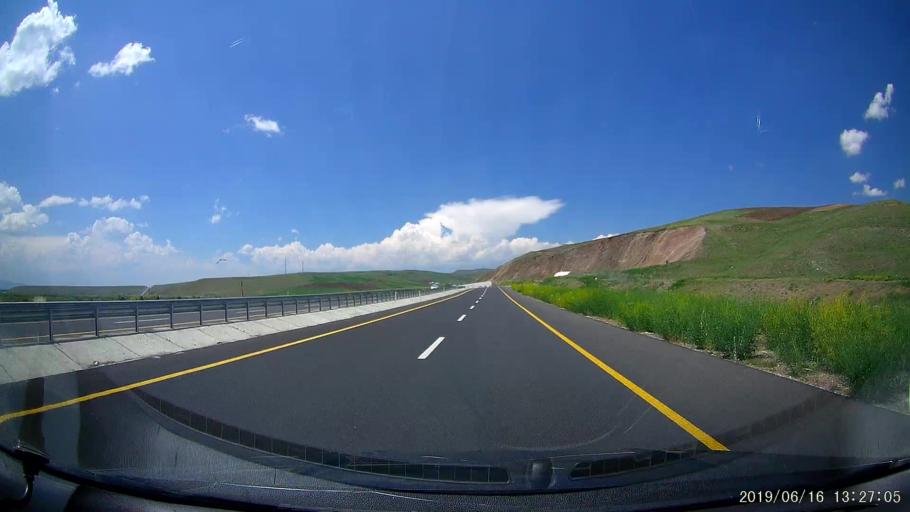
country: TR
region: Agri
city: Taslicay
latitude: 39.6664
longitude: 43.3163
